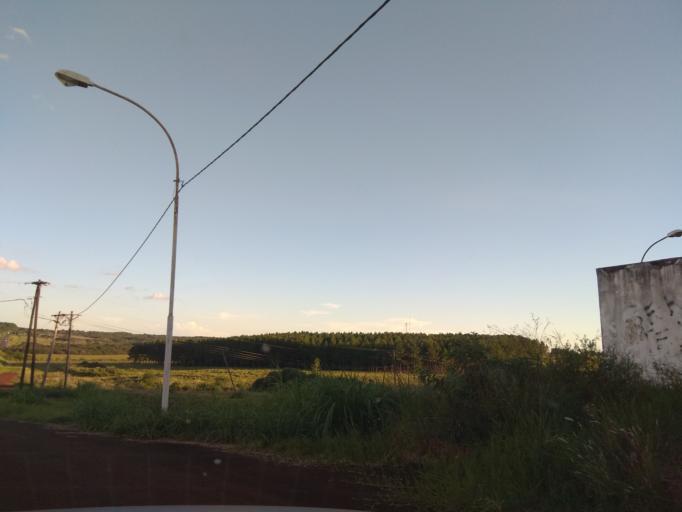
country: AR
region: Misiones
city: Garupa
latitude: -27.5940
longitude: -55.8346
